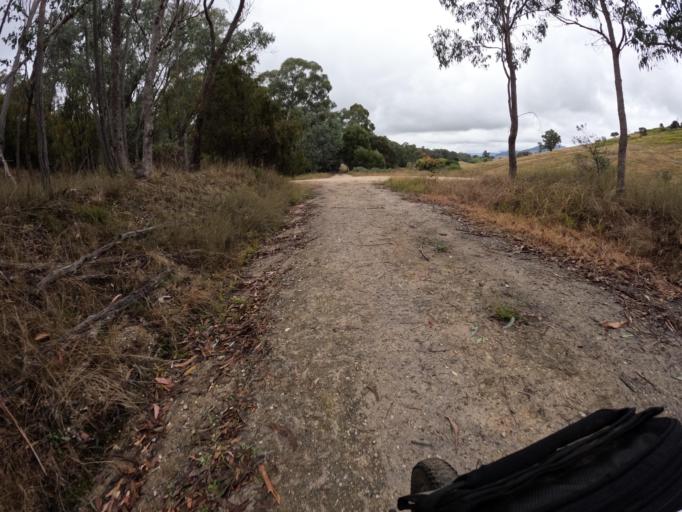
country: AU
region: New South Wales
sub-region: Greater Hume Shire
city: Holbrook
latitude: -36.1576
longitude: 147.4104
